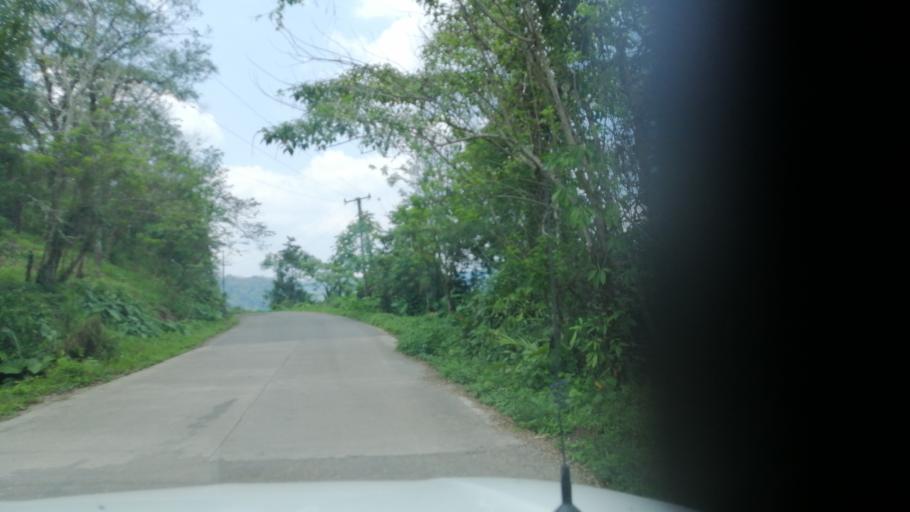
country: MX
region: Chiapas
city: Ostuacan
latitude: 17.3989
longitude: -93.3318
